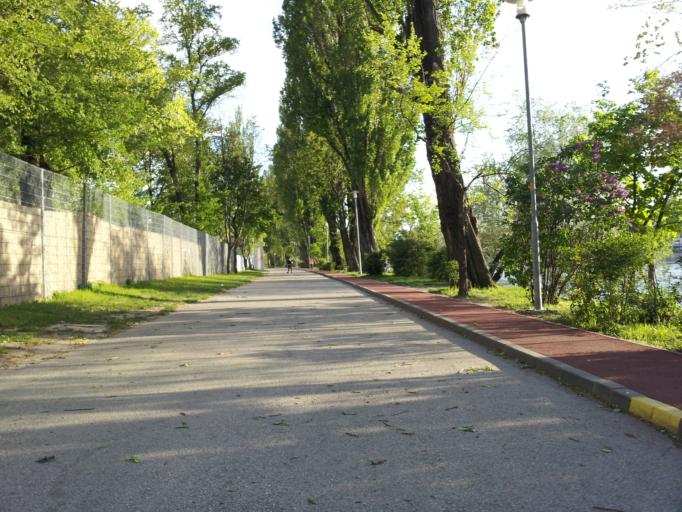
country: HU
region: Budapest
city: Budapest II. keruelet
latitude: 47.5234
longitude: 19.0426
